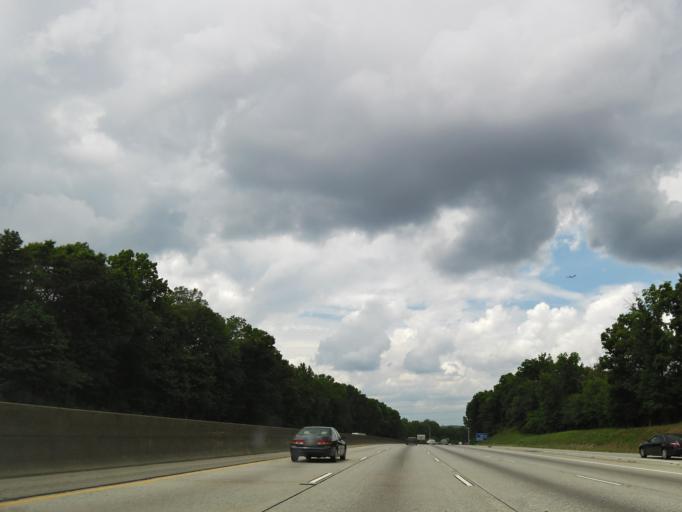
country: US
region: Georgia
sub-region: Fulton County
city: College Park
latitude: 33.6396
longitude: -84.4944
